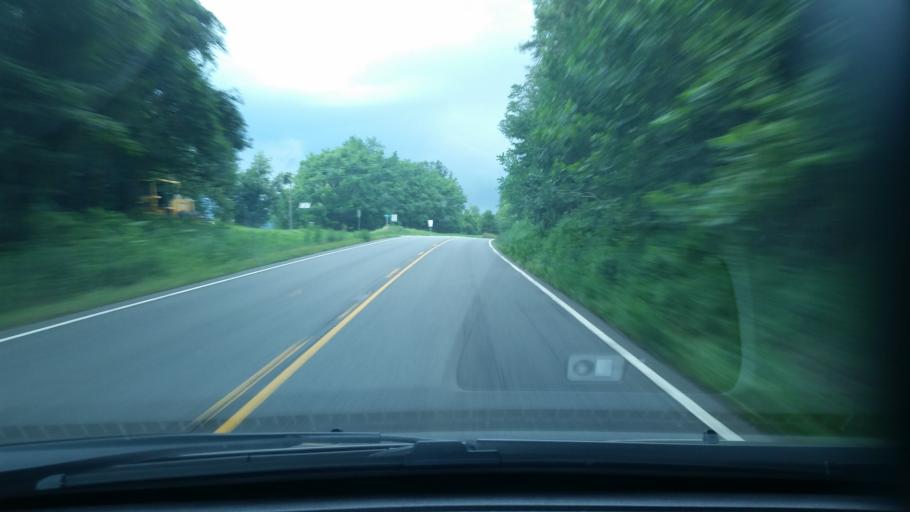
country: US
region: Virginia
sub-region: Nelson County
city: Nellysford
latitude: 37.8692
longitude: -78.8201
